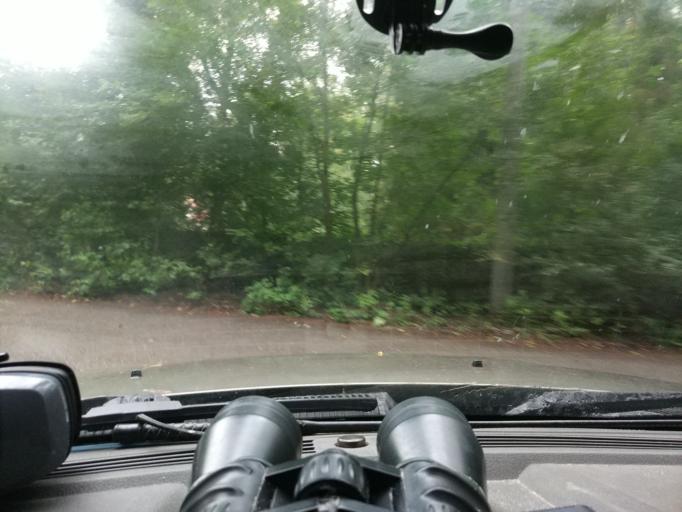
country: PL
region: Masovian Voivodeship
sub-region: Powiat grodziski
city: Podkowa Lesna
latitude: 52.1278
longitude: 20.7365
